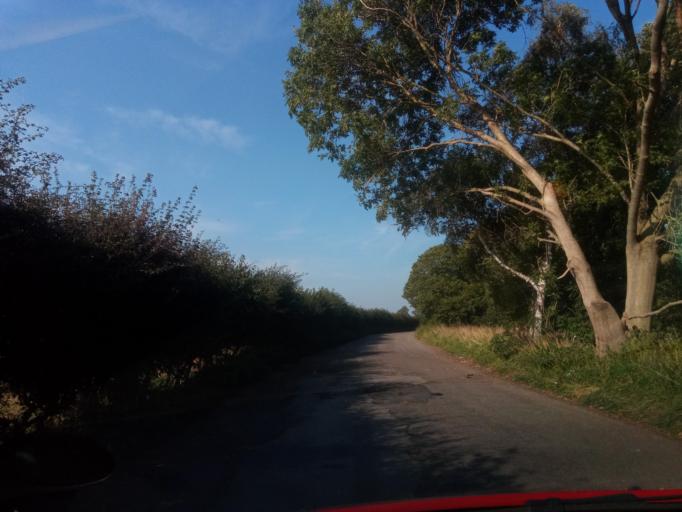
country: GB
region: England
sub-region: North Yorkshire
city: Raskelf
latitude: 54.1475
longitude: -1.2389
